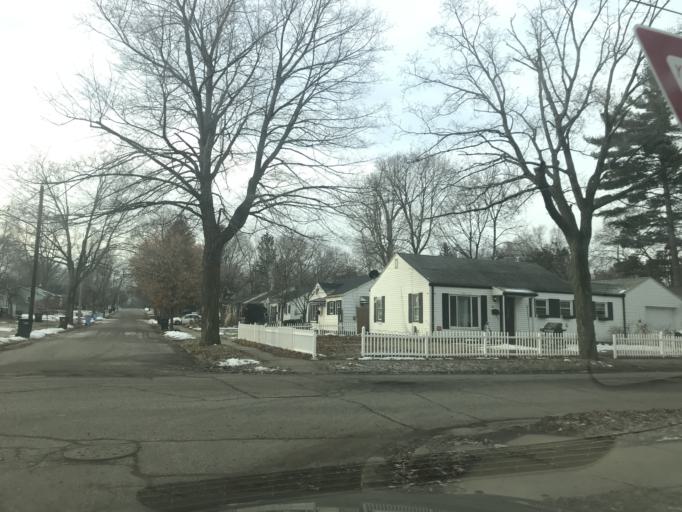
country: US
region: Michigan
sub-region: Ingham County
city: Edgemont Park
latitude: 42.7530
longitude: -84.5701
